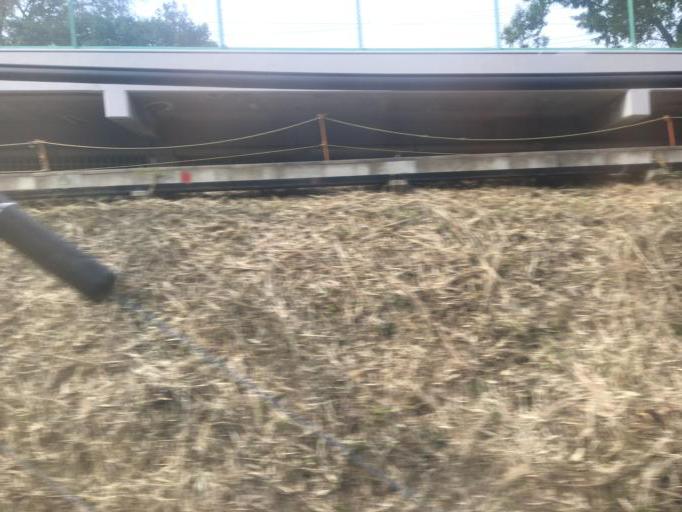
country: JP
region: Saitama
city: Sayama
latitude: 35.8314
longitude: 139.4102
